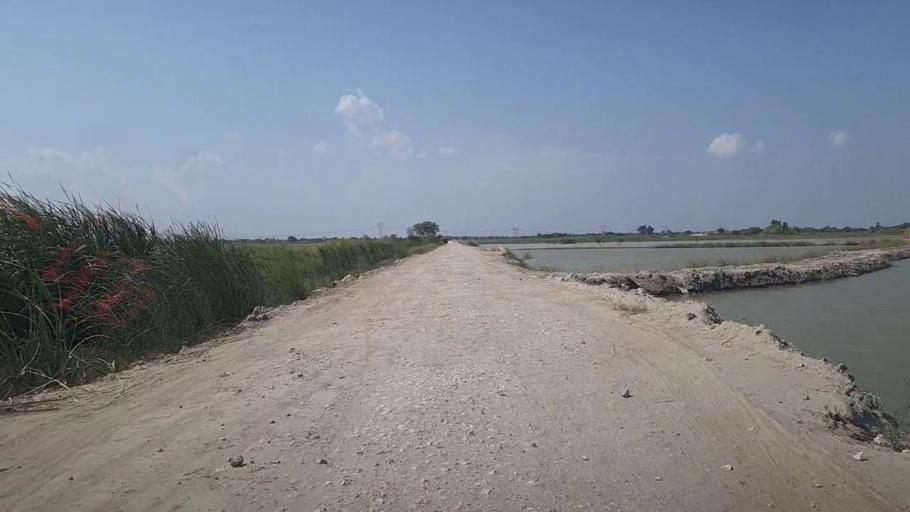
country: PK
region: Sindh
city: Khairpur
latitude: 28.0981
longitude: 69.6270
